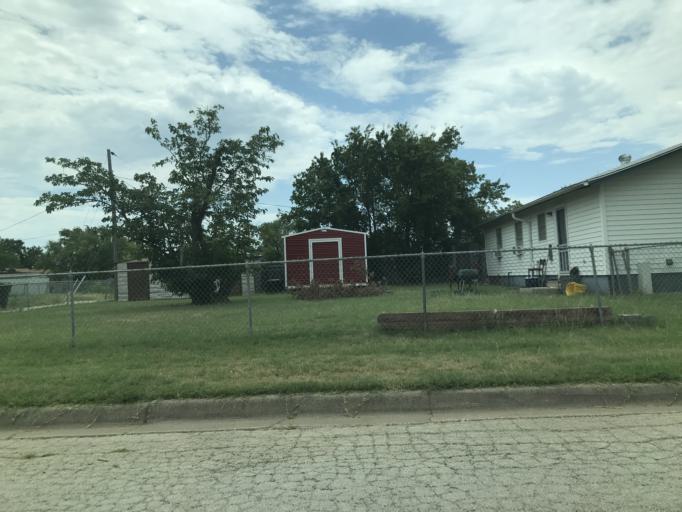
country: US
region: Texas
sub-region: Taylor County
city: Abilene
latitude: 32.4520
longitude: -99.6974
